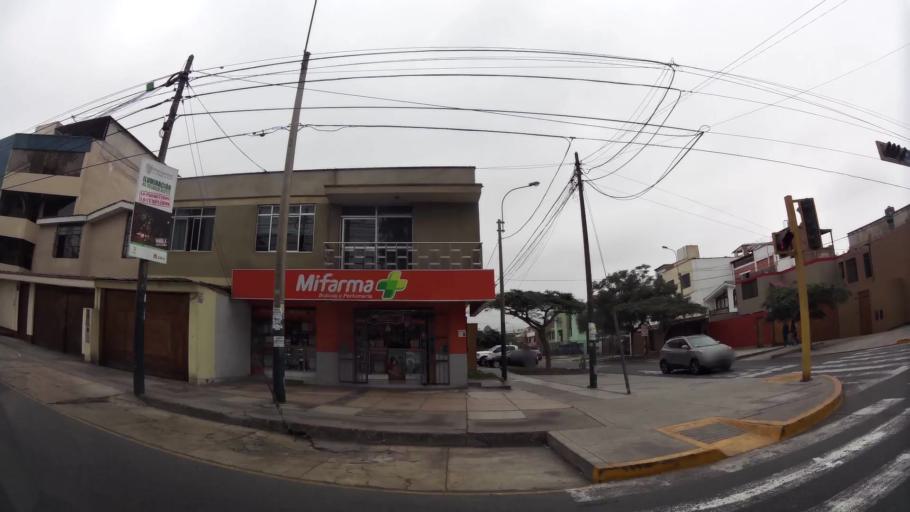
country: PE
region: Lima
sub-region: Lima
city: Surco
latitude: -12.1340
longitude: -76.9898
